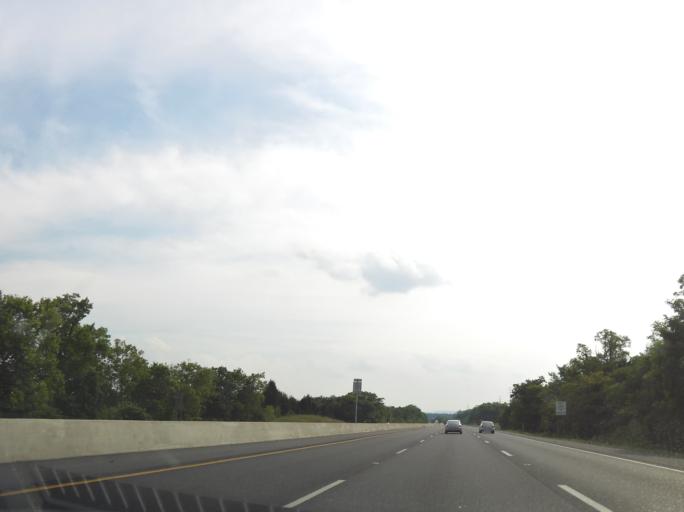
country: US
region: Maryland
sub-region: Washington County
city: Williamsport
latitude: 39.5645
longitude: -77.8945
